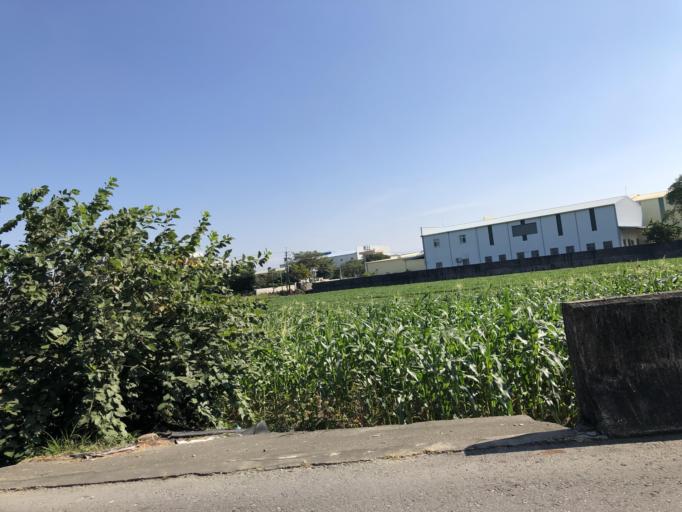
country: TW
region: Taiwan
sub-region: Tainan
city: Tainan
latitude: 23.0228
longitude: 120.2895
